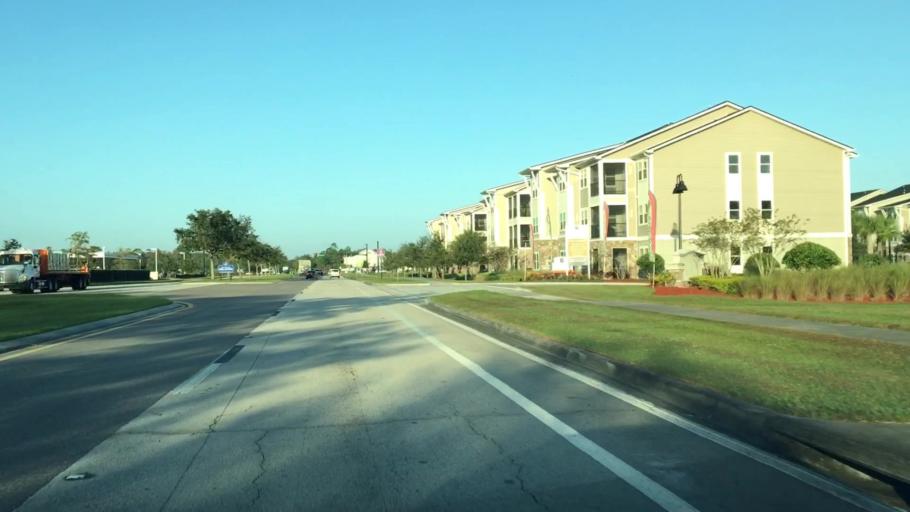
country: US
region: Florida
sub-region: Orange County
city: Azalea Park
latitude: 28.4782
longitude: -81.2444
